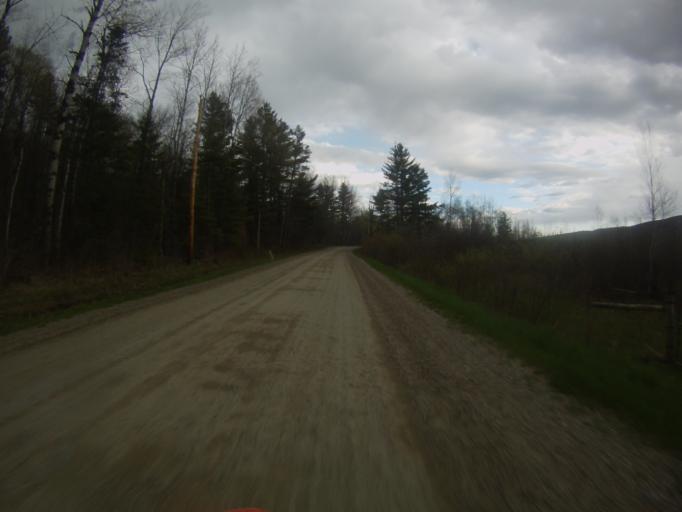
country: US
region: Vermont
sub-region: Addison County
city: Bristol
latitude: 44.0410
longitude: -73.0150
